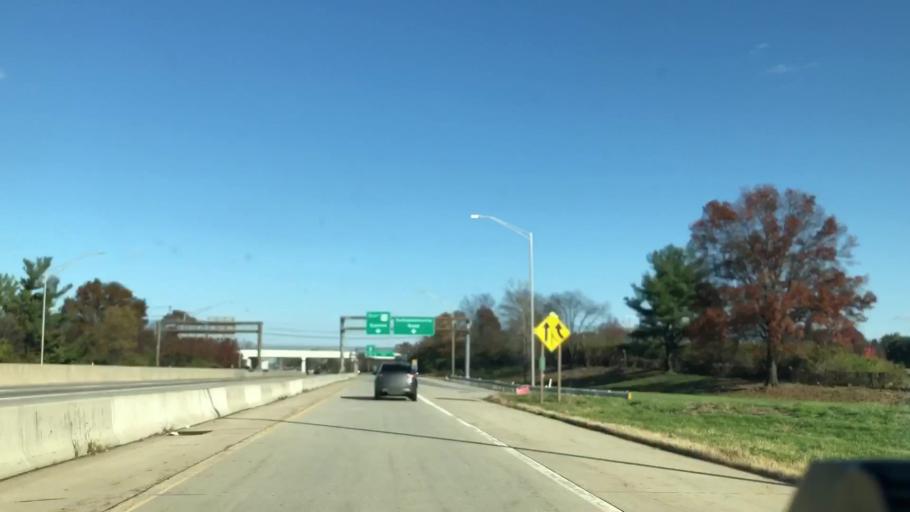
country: US
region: Pennsylvania
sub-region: Northampton County
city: Bethlehem
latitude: 40.6489
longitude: -75.4138
